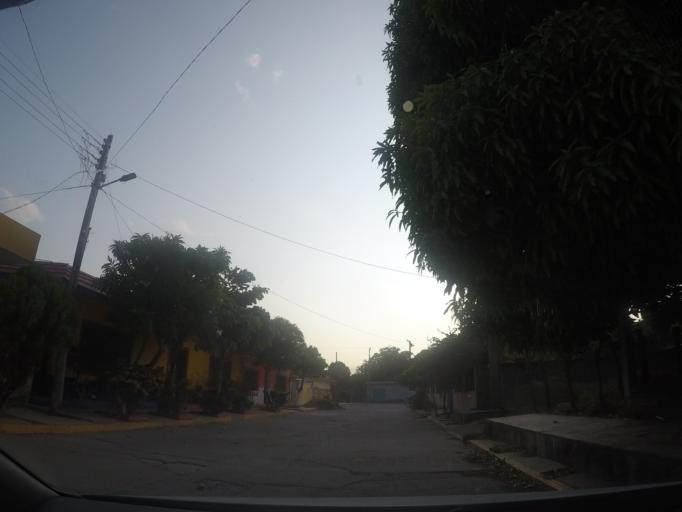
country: MX
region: Oaxaca
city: San Jeronimo Ixtepec
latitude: 16.5918
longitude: -95.1632
